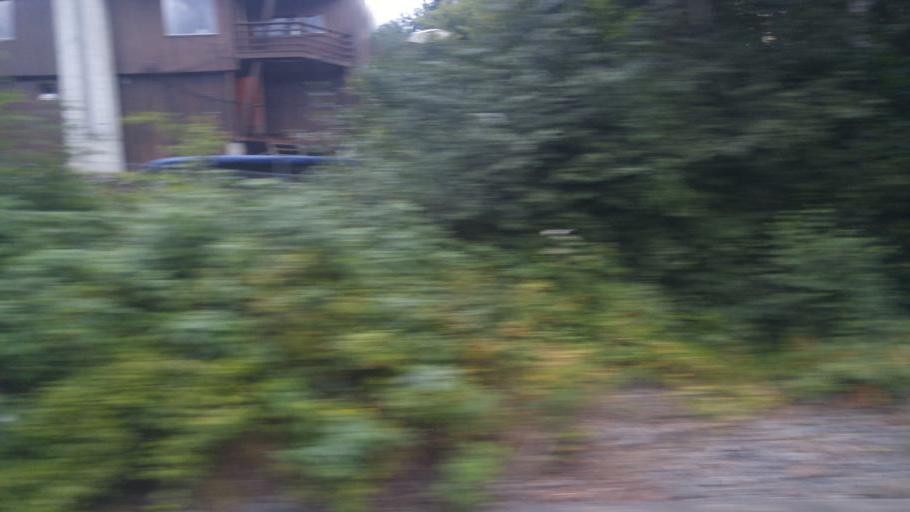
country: NO
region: Oslo
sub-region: Oslo
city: Sjolyststranda
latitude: 59.9579
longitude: 10.6962
